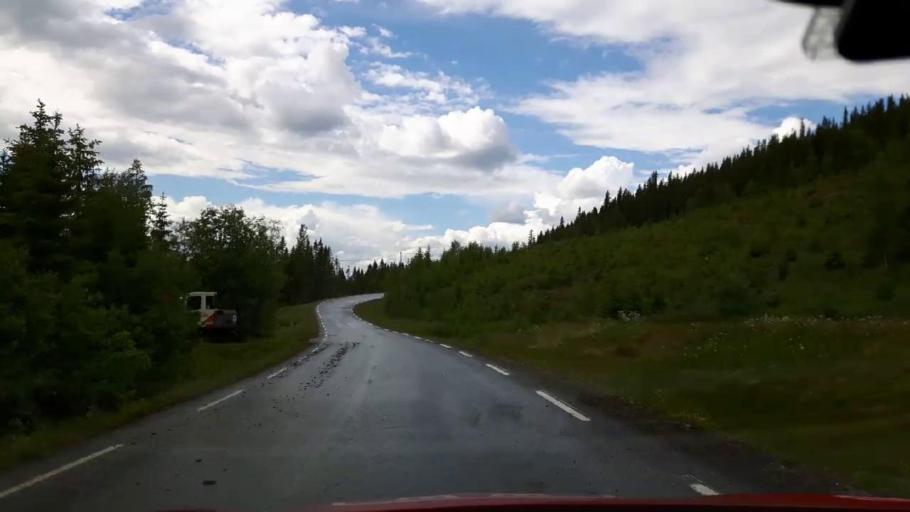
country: NO
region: Nord-Trondelag
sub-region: Lierne
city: Sandvika
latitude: 64.1020
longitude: 14.0031
